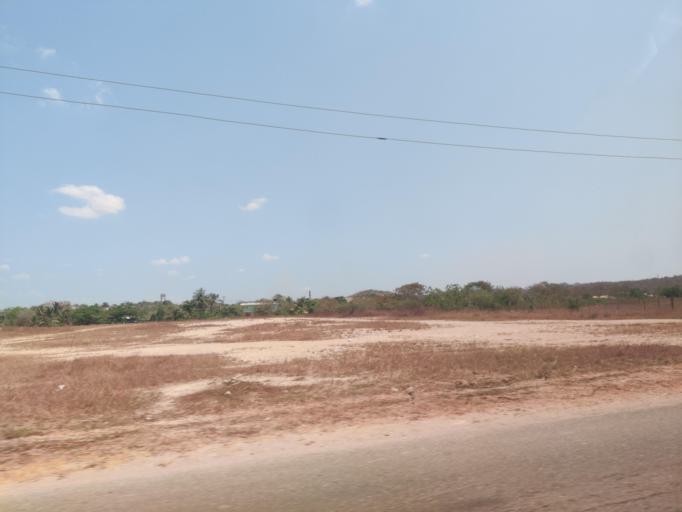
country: CO
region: Bolivar
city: Turbana
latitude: 10.2764
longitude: -75.5143
